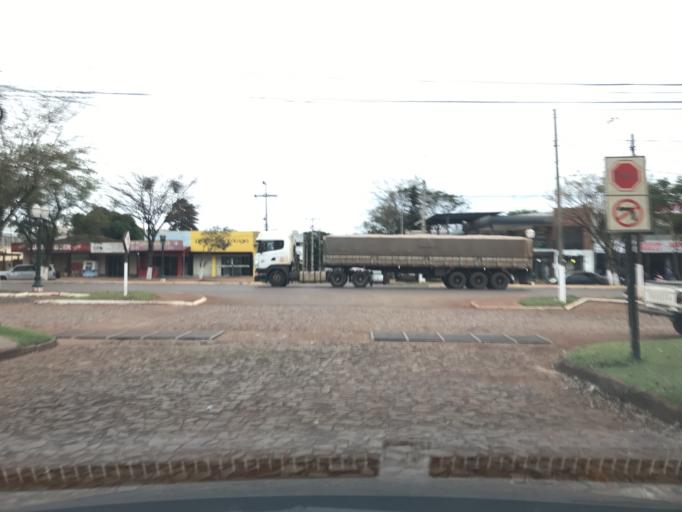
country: PY
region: Canindeyu
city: Colonia Catuete
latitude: -24.2471
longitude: -54.7601
